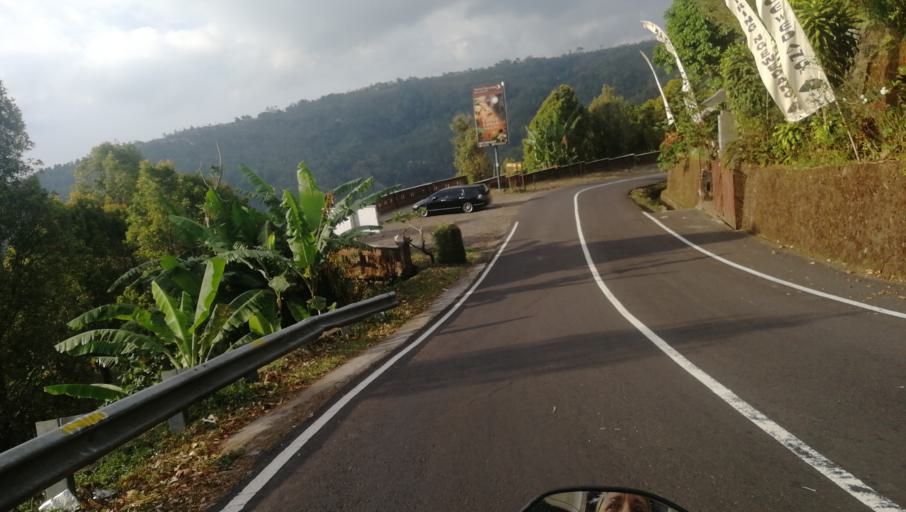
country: ID
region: Bali
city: Munduk
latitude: -8.2584
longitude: 115.0746
